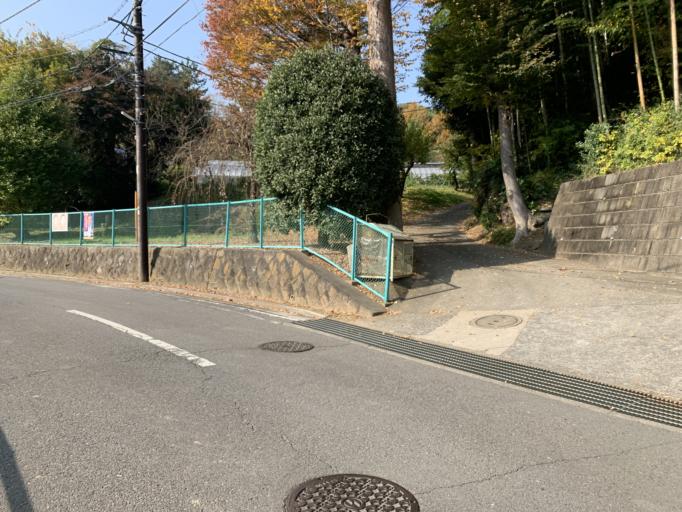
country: JP
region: Tokyo
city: Kokubunji
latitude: 35.6275
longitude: 139.4762
